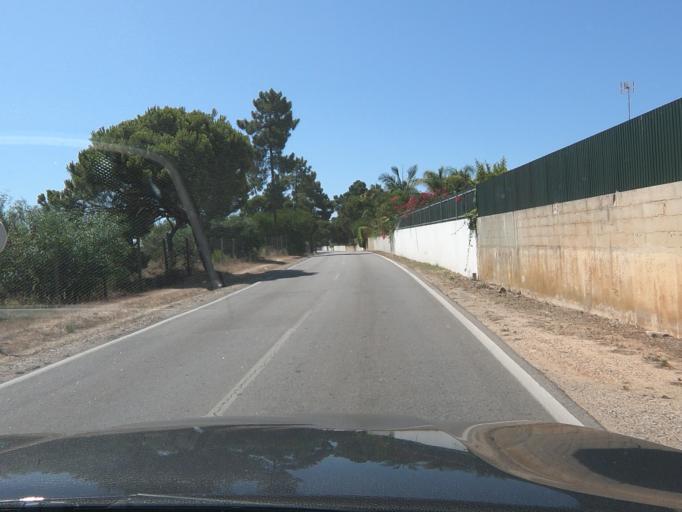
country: PT
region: Faro
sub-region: Loule
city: Vilamoura
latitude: 37.0840
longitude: -8.1005
